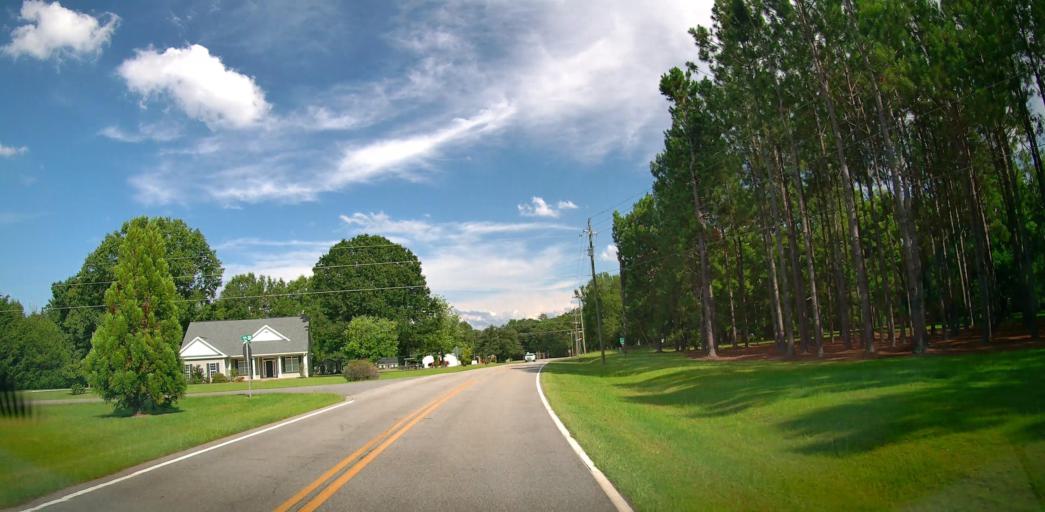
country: US
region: Georgia
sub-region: Houston County
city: Robins Air Force Base
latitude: 32.5318
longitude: -83.6344
